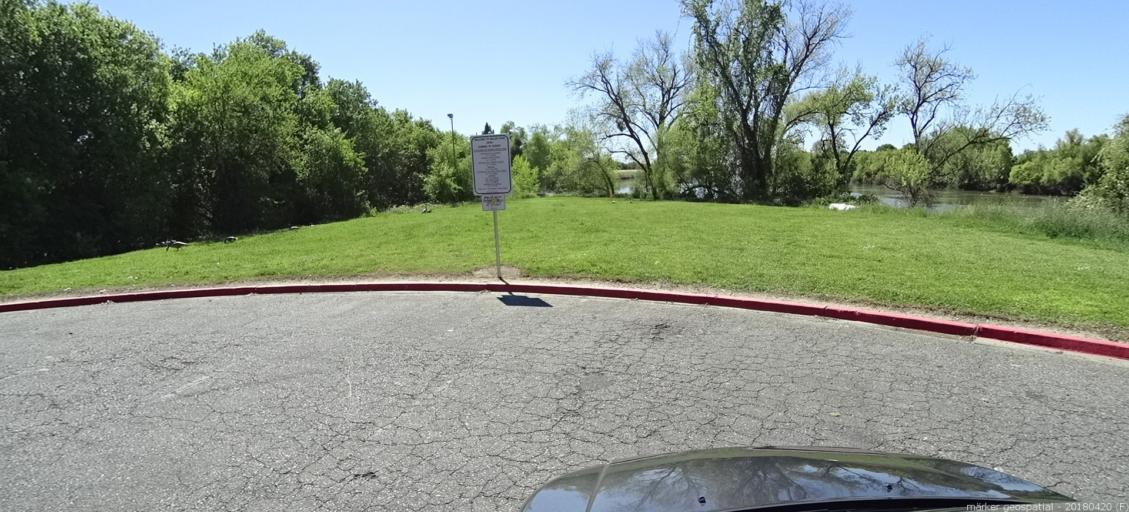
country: US
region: California
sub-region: Yolo County
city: West Sacramento
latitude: 38.5615
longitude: -121.5173
